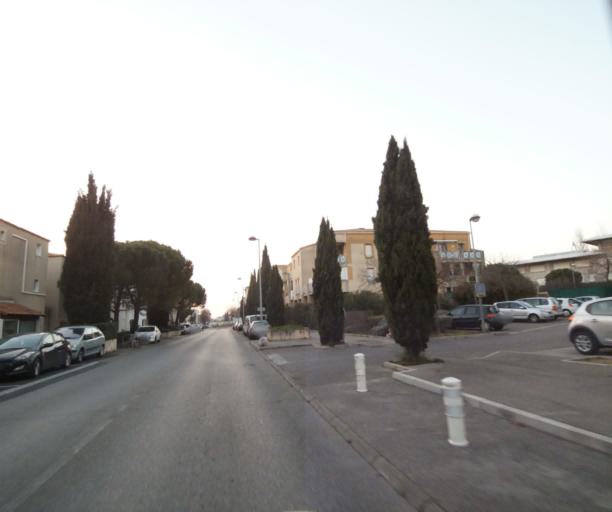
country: FR
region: Provence-Alpes-Cote d'Azur
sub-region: Departement des Bouches-du-Rhone
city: Saint-Victoret
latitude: 43.4235
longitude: 5.2729
